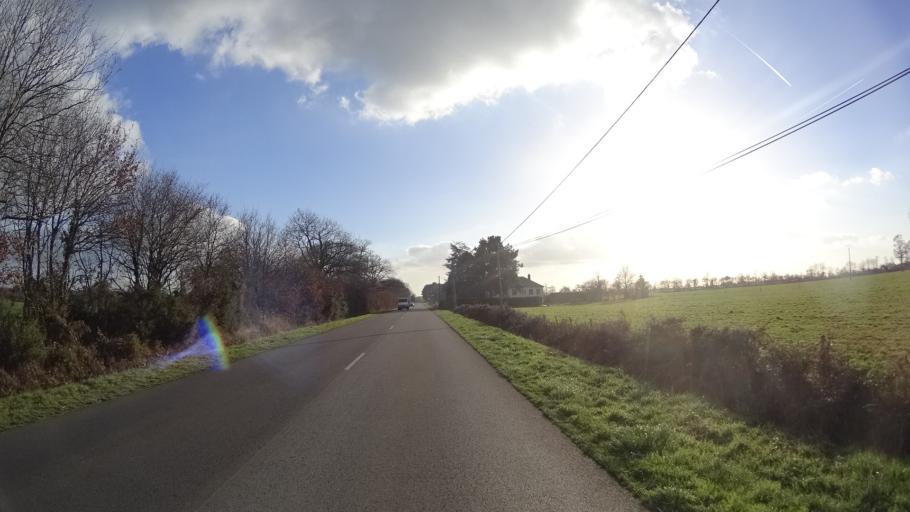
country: FR
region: Pays de la Loire
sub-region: Departement de la Loire-Atlantique
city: Plesse
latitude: 47.5189
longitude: -1.8864
